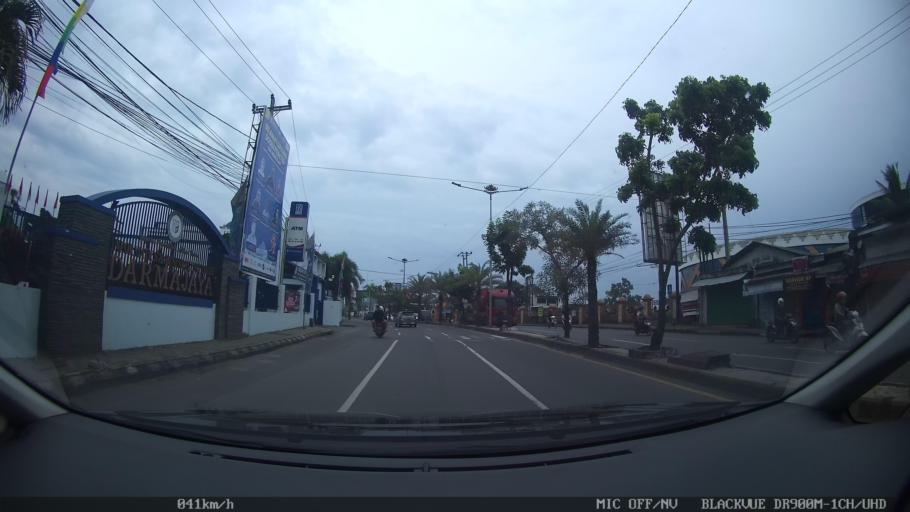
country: ID
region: Lampung
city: Kedaton
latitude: -5.3772
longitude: 105.2503
